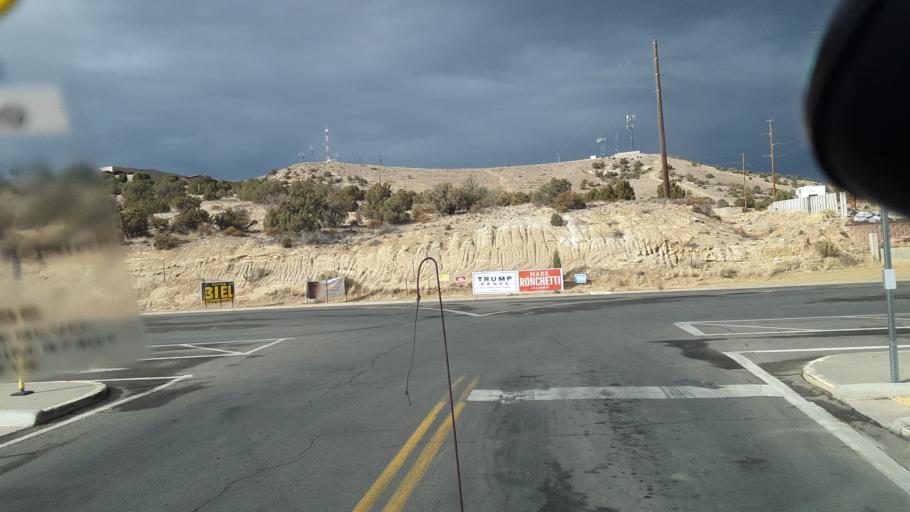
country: US
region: New Mexico
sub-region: San Juan County
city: Farmington
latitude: 36.7740
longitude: -108.1855
